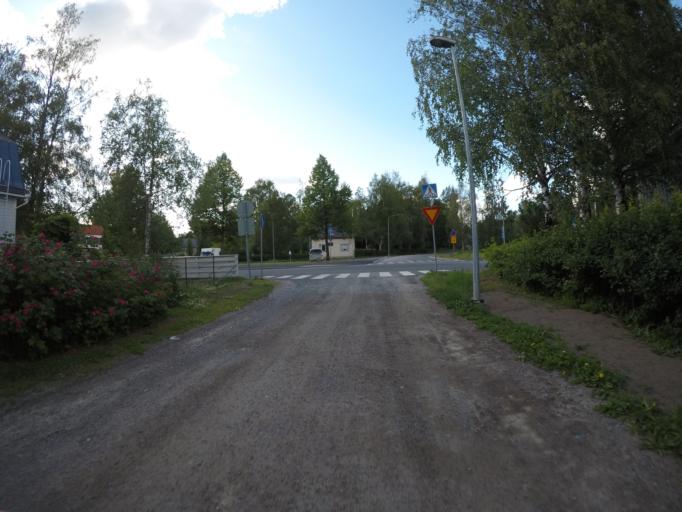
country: FI
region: Haeme
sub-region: Haemeenlinna
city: Haemeenlinna
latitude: 61.0079
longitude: 24.4976
